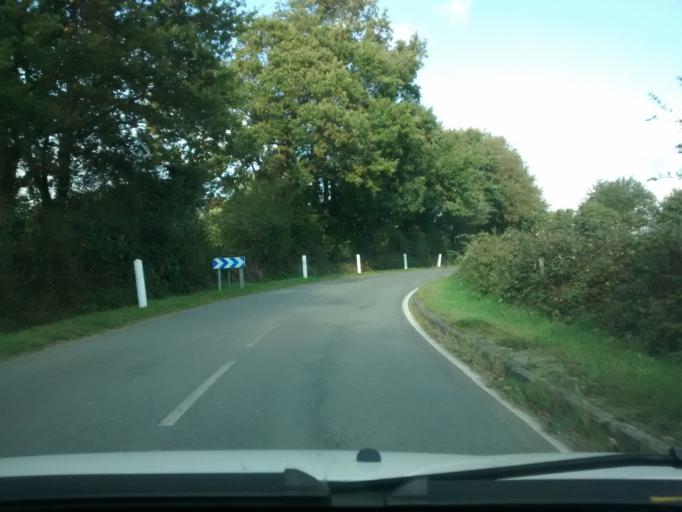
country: FR
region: Pays de la Loire
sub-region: Departement de la Loire-Atlantique
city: Sautron
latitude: 47.2879
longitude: -1.6596
